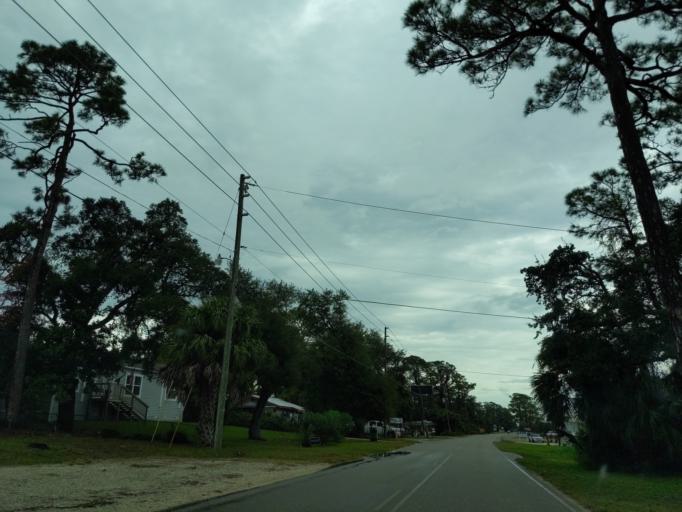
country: US
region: Florida
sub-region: Franklin County
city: Eastpoint
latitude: 29.7349
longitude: -84.8818
